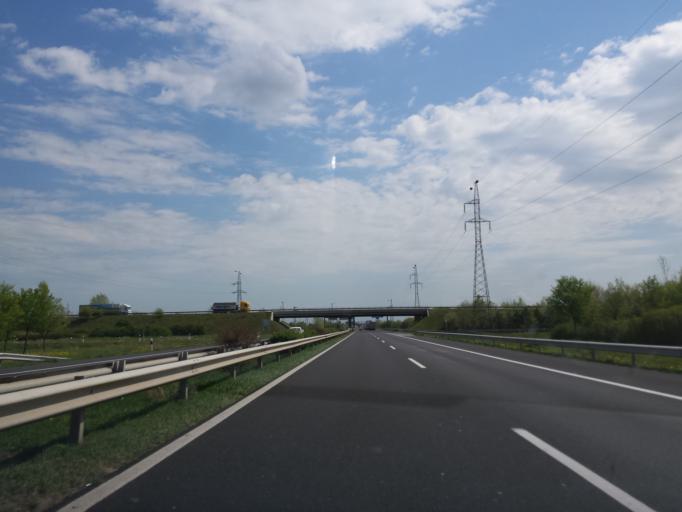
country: HU
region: Gyor-Moson-Sopron
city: Mosonmagyarovar
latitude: 47.8528
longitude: 17.2466
